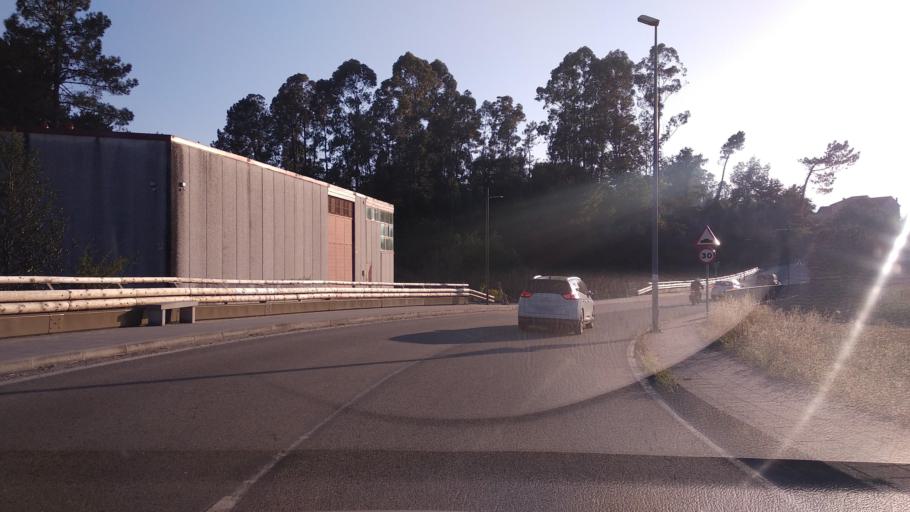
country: ES
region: Galicia
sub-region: Provincia de Pontevedra
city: Redondela
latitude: 42.3394
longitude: -8.5957
